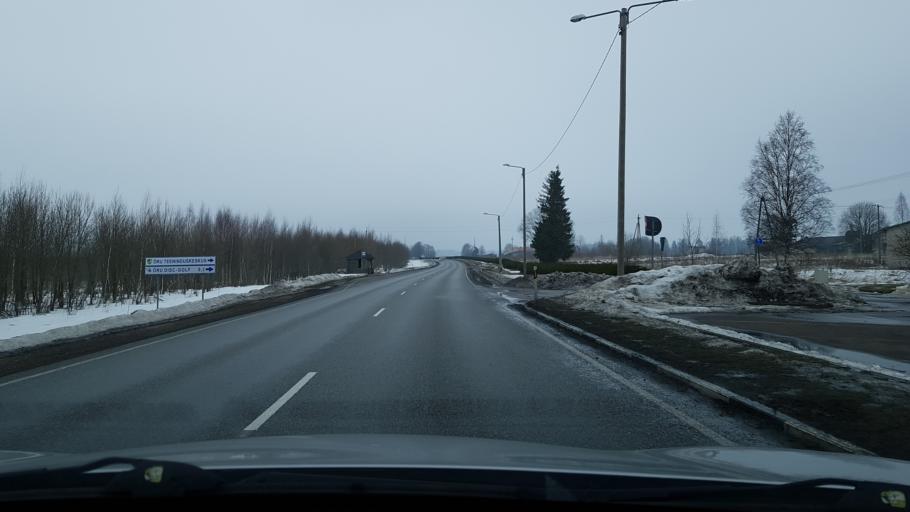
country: EE
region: Valgamaa
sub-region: Valga linn
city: Valga
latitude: 57.9264
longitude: 26.1757
